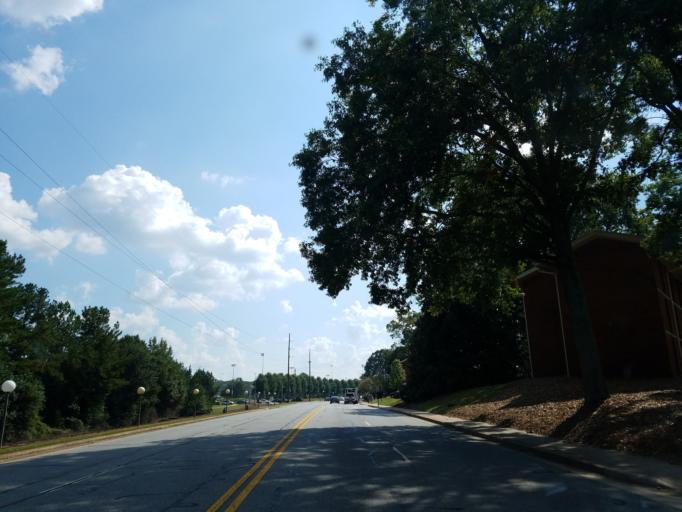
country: US
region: Georgia
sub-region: Clarke County
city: Athens
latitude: 33.9374
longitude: -83.3733
